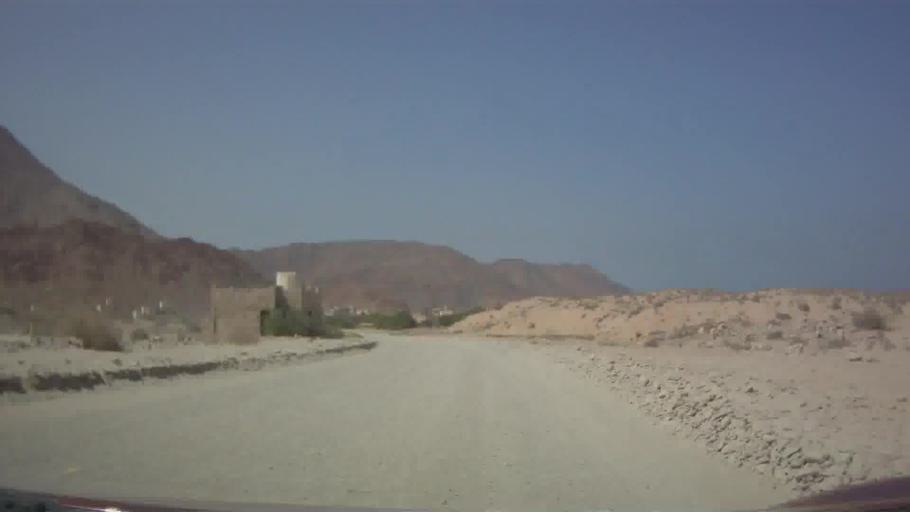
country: OM
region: Muhafazat Masqat
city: Muscat
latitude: 23.4199
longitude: 58.7852
